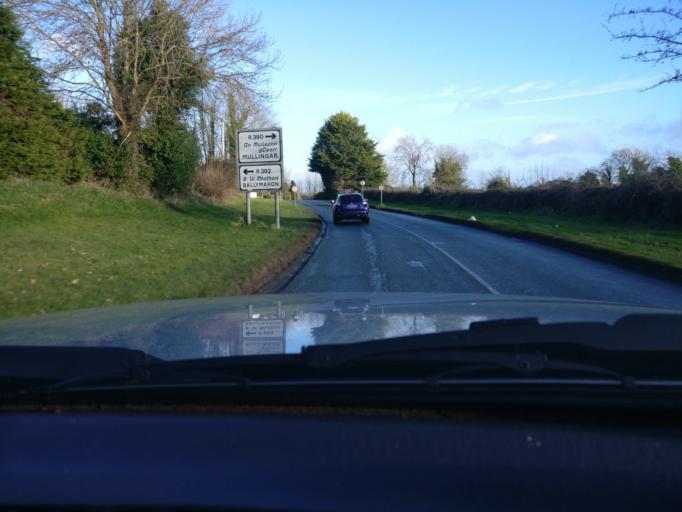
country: IE
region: Leinster
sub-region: An Iarmhi
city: An Muileann gCearr
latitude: 53.5159
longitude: -7.3770
